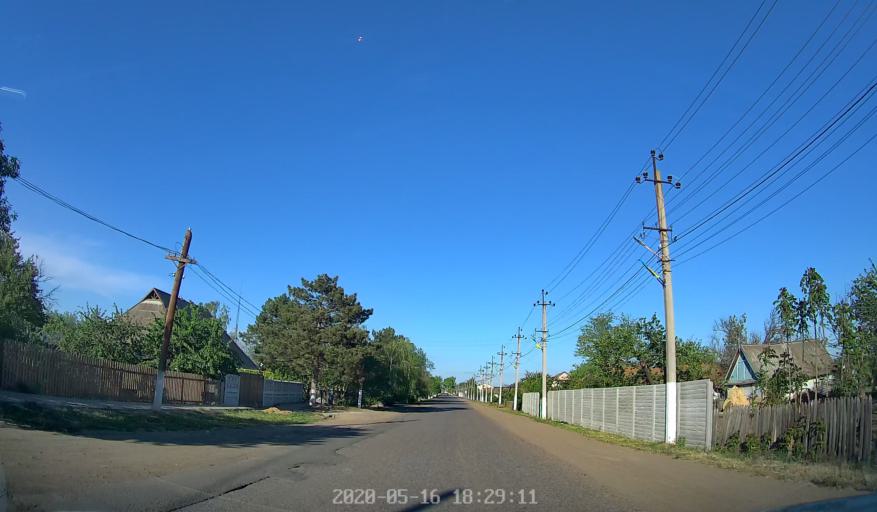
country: MD
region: Telenesti
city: Dnestrovsc
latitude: 46.5358
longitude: 30.0165
